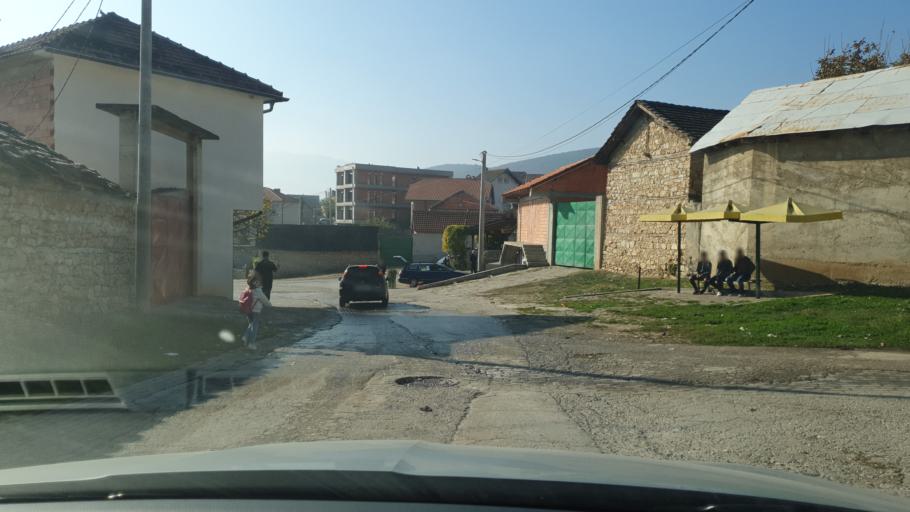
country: MK
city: Bojane
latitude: 42.0003
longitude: 21.1929
